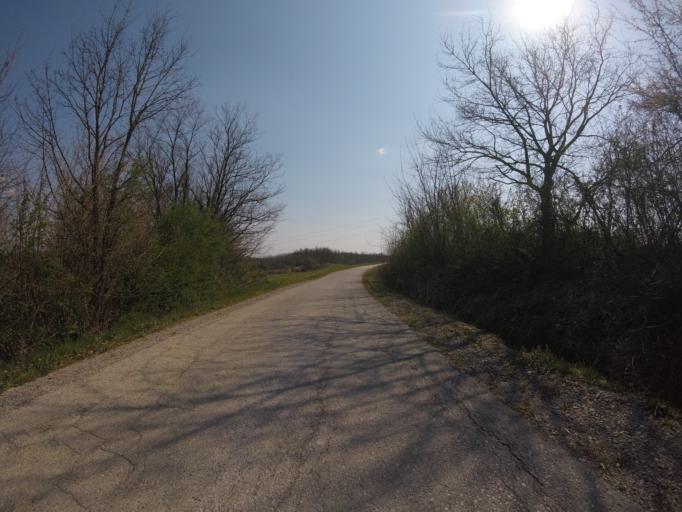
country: HR
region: Grad Zagreb
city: Strmec
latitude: 45.5524
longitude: 15.9023
